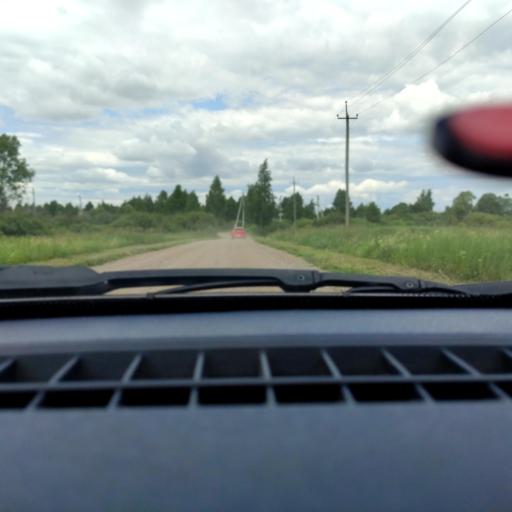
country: RU
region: Bashkortostan
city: Kabakovo
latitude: 54.7292
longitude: 56.2025
